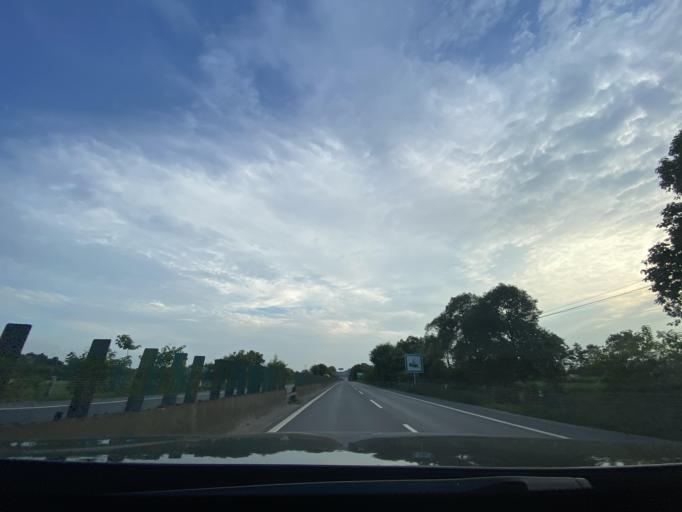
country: CN
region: Sichuan
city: Luojiang
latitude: 31.3686
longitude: 104.5408
